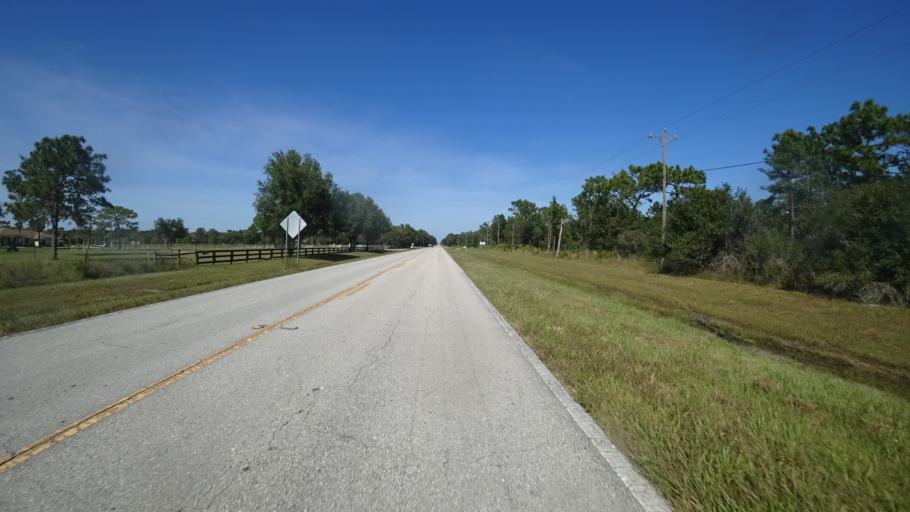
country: US
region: Florida
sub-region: Sarasota County
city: The Meadows
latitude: 27.4033
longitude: -82.3040
